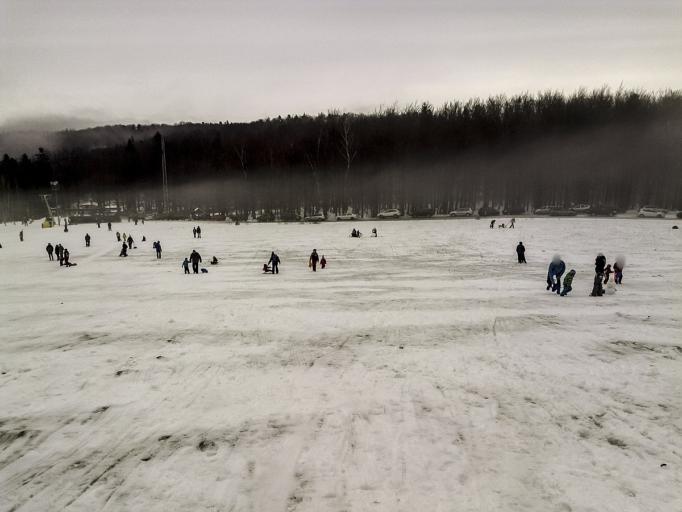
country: SK
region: Kosicky
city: Kosice
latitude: 48.7660
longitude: 21.1304
